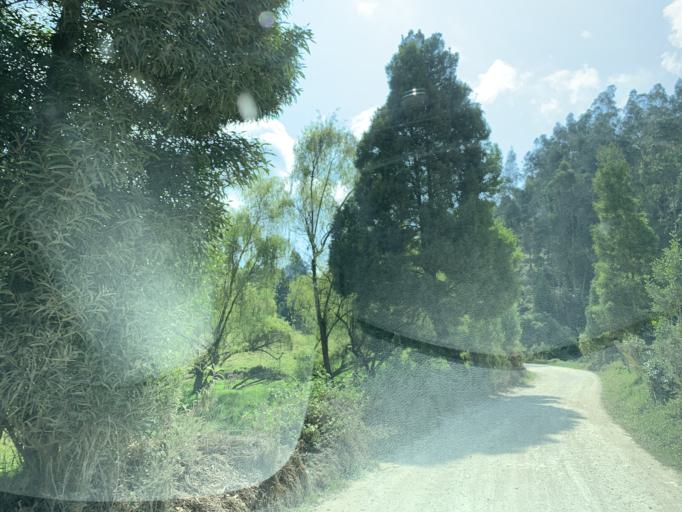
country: CO
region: Boyaca
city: Turmeque
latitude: 5.2794
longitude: -73.5038
